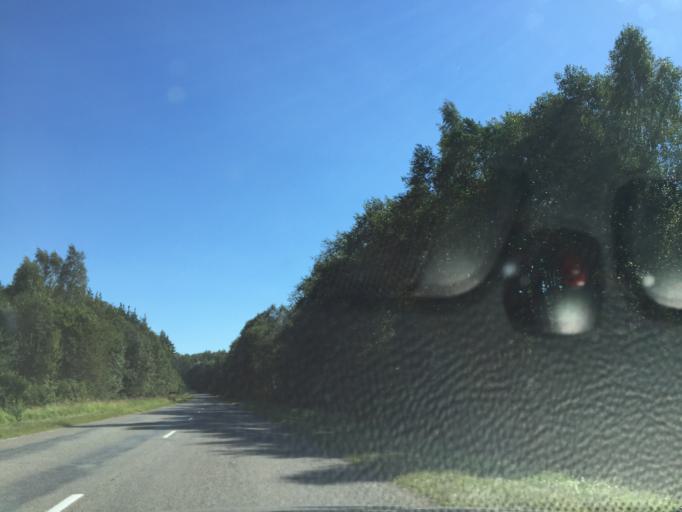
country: LV
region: Akniste
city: Akniste
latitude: 56.1191
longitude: 25.8319
